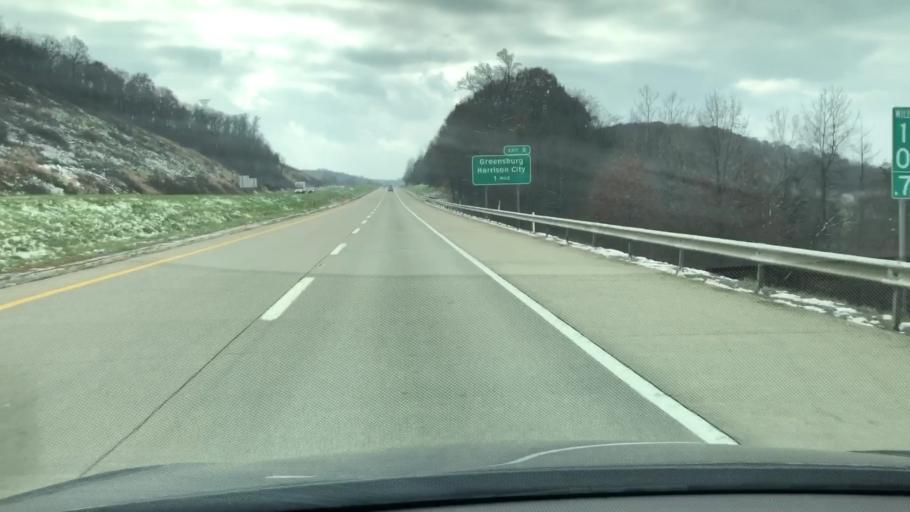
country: US
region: Pennsylvania
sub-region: Westmoreland County
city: Delmont
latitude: 40.3619
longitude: -79.5583
